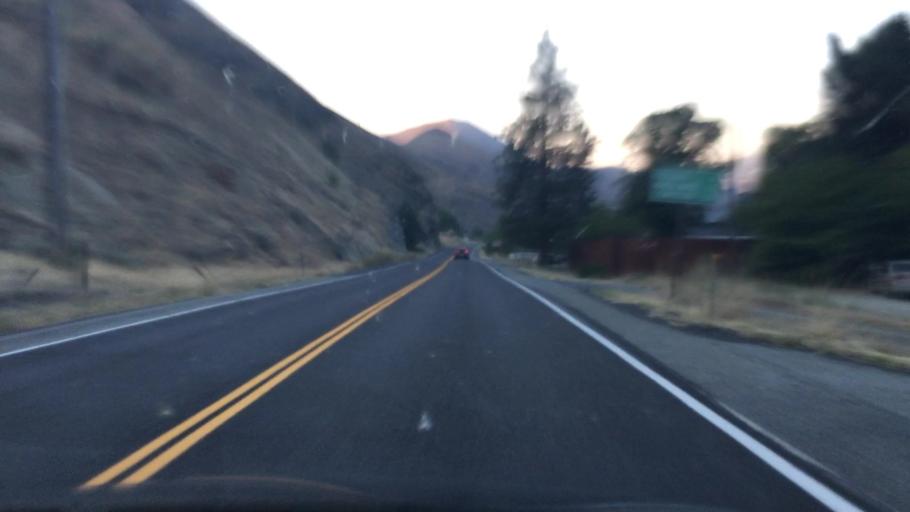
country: US
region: Idaho
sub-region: Valley County
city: McCall
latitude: 45.3678
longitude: -116.3592
